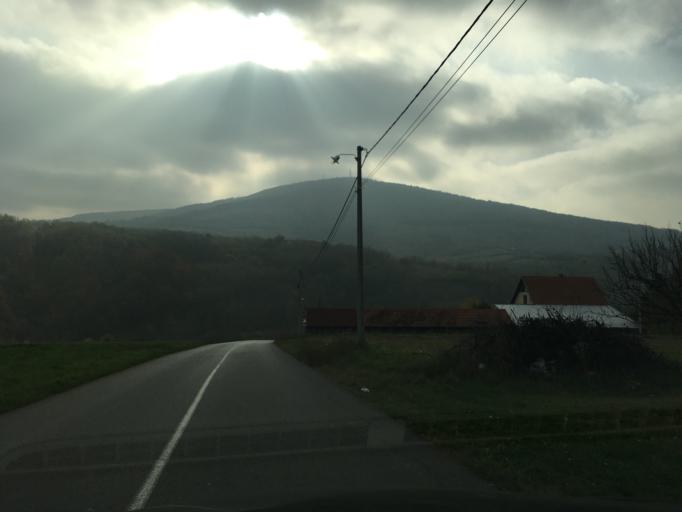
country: RS
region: Central Serbia
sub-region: Belgrade
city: Sopot
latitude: 44.4924
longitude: 20.5924
